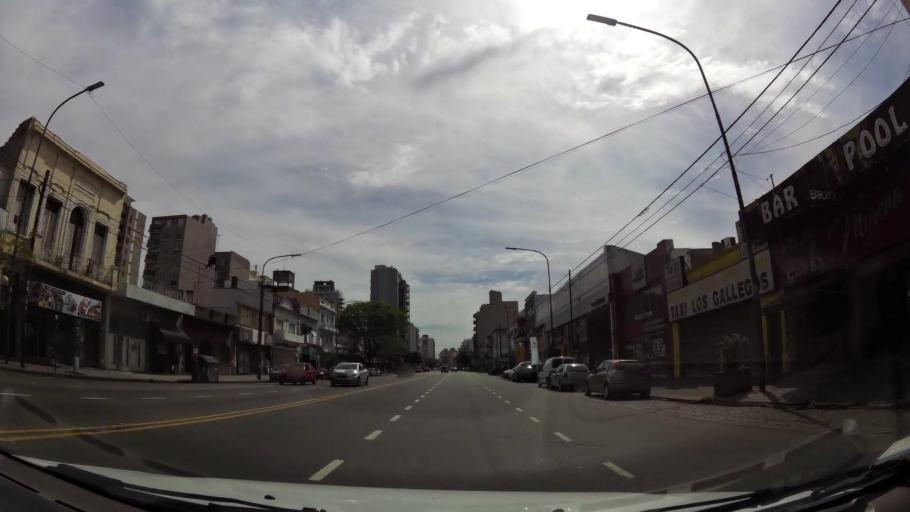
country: AR
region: Buenos Aires F.D.
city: Villa Santa Rita
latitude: -34.6382
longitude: -58.5050
